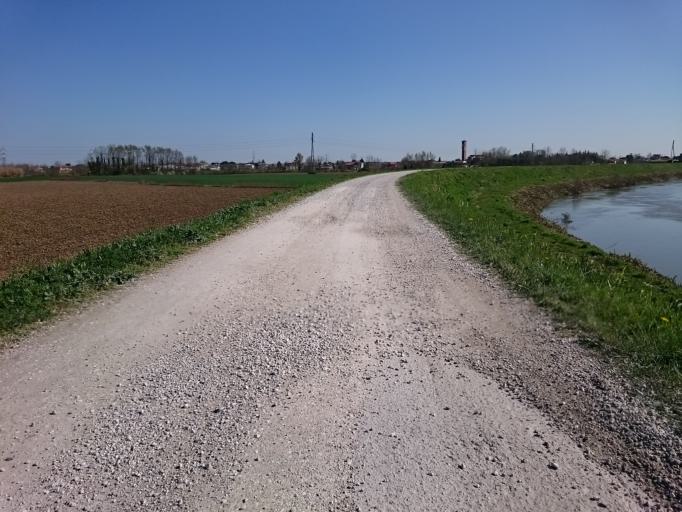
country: IT
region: Veneto
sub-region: Provincia di Padova
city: Ponte San Nicolo
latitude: 45.3745
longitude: 11.9316
